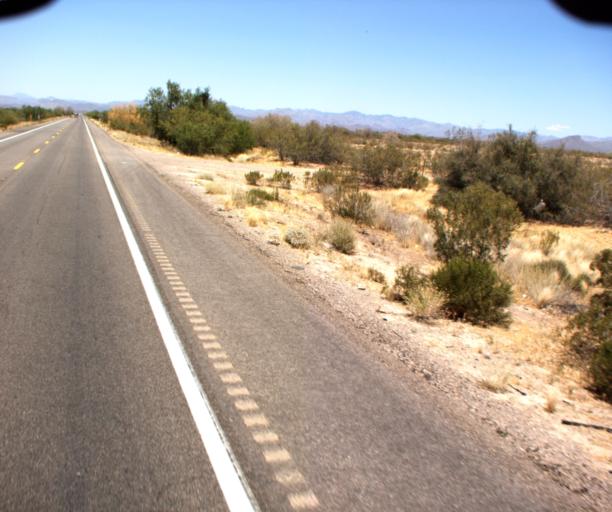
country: US
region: Arizona
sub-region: Pinal County
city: Gold Camp
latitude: 33.1892
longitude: -111.3505
